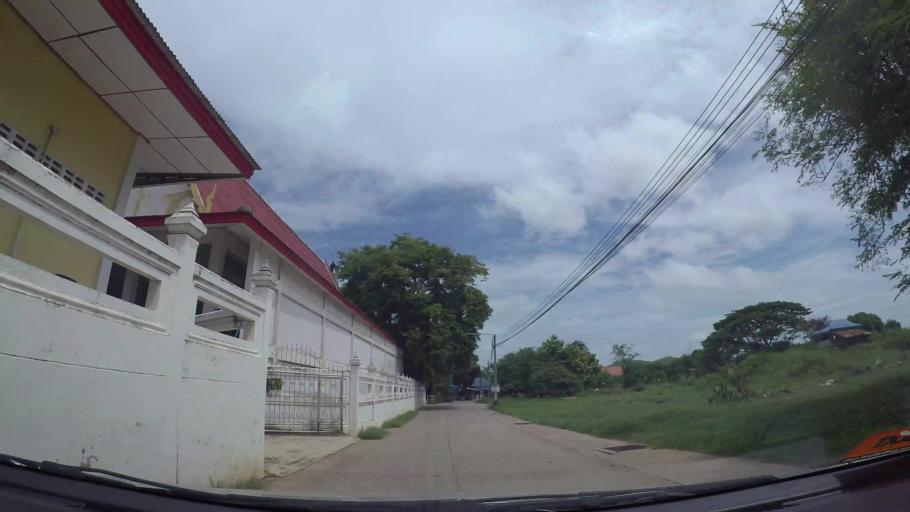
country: TH
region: Chon Buri
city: Sattahip
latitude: 12.6808
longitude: 100.9015
